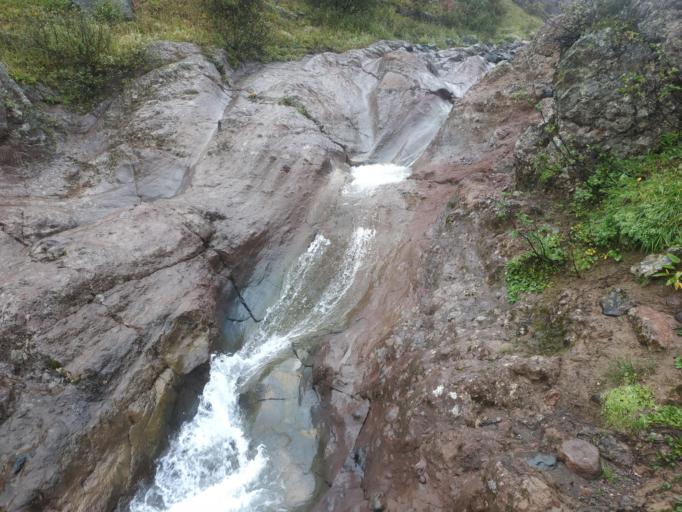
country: RU
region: Kamtsjatka
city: Petropavlovsk-Kamchatsky
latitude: 53.5919
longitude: 158.9212
